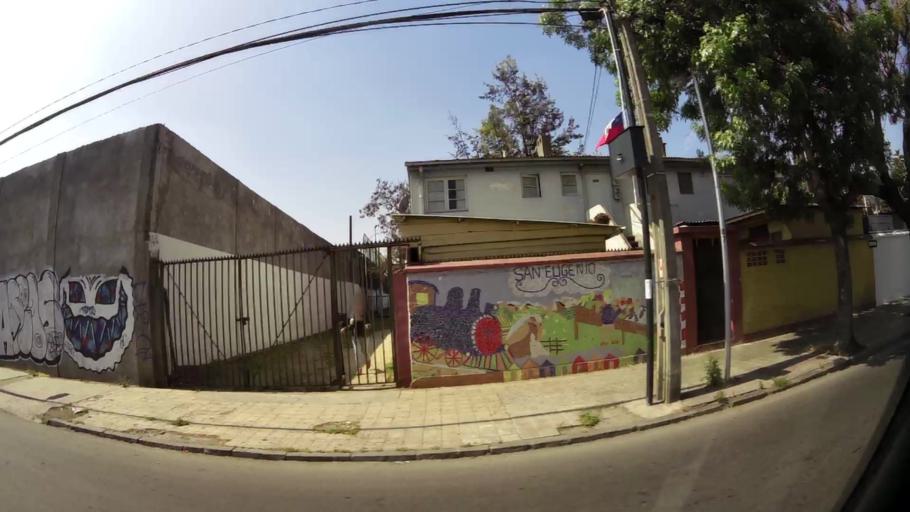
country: CL
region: Santiago Metropolitan
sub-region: Provincia de Santiago
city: Santiago
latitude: -33.4645
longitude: -70.6734
